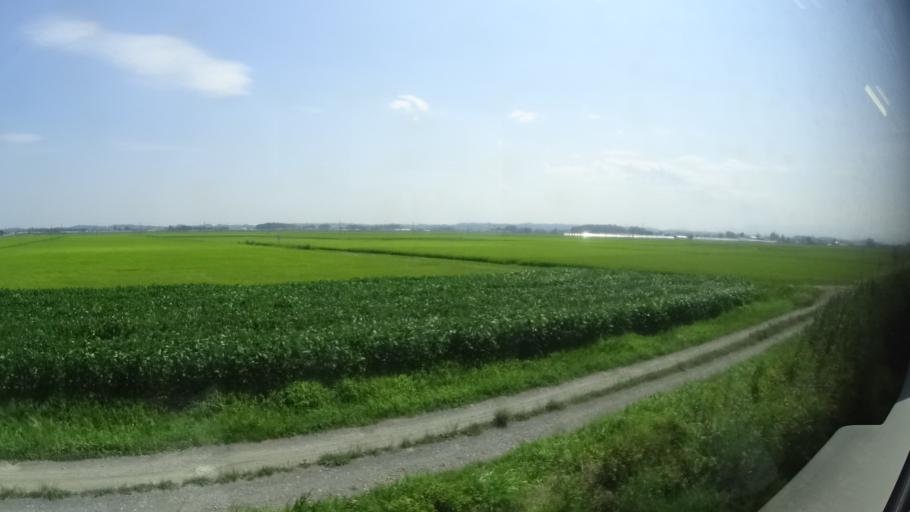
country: JP
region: Miyagi
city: Wakuya
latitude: 38.5503
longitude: 141.0929
